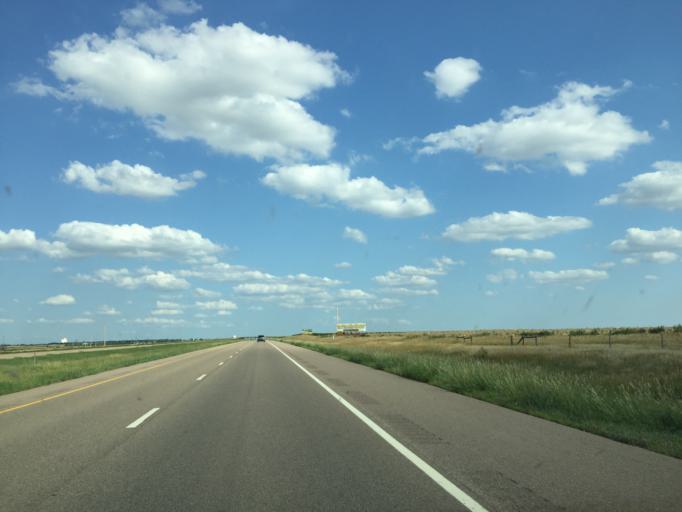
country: US
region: Kansas
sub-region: Gove County
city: Gove
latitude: 39.0830
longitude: -100.2954
